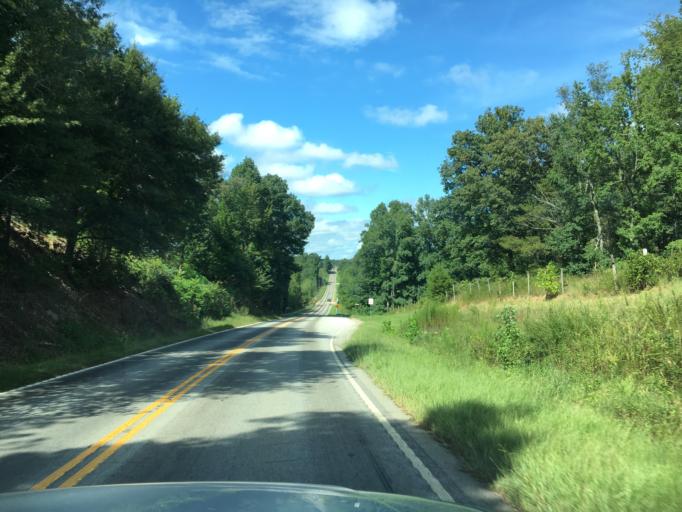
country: US
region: South Carolina
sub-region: Spartanburg County
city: Inman Mills
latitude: 35.0020
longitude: -82.1123
